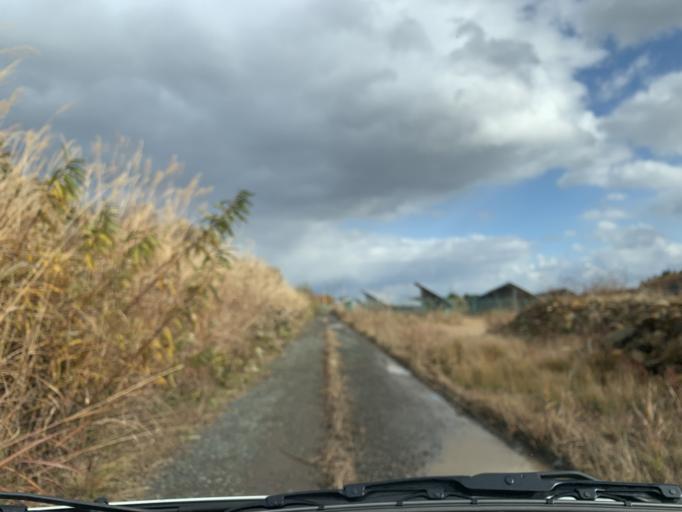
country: JP
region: Iwate
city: Mizusawa
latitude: 39.1121
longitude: 140.9531
